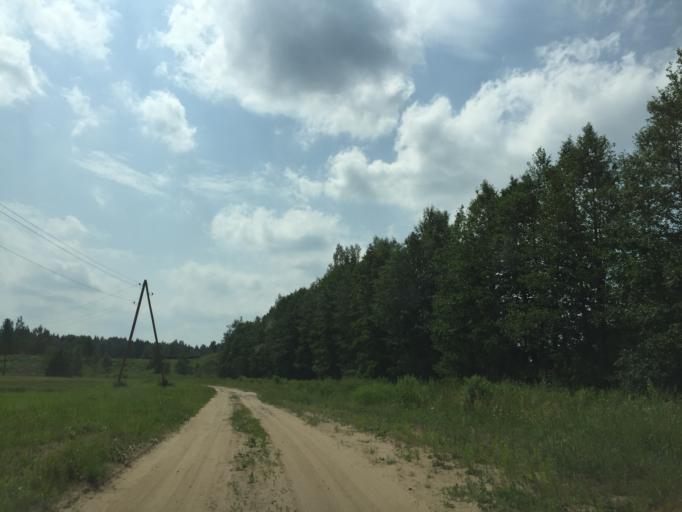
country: LV
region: Olaine
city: Olaine
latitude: 56.7738
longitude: 23.9152
